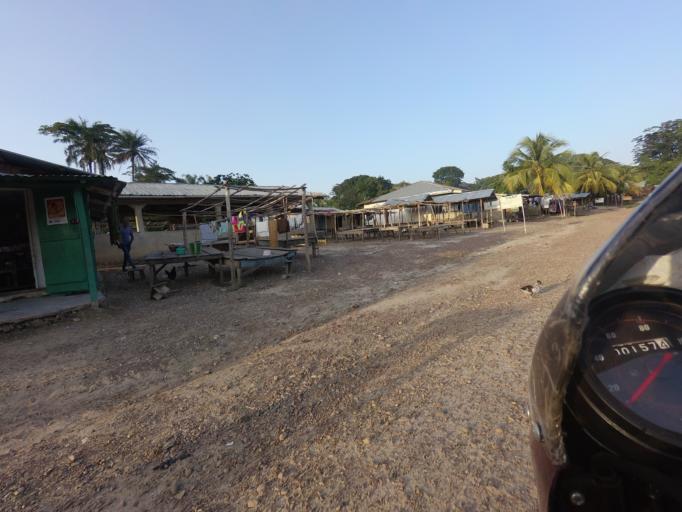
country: SL
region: Eastern Province
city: Tombu
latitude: 8.4149
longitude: -10.7199
